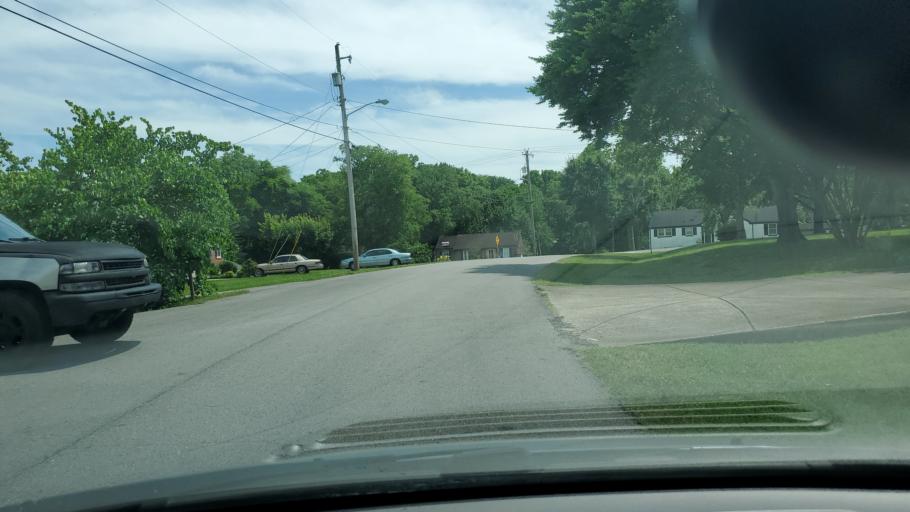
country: US
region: Tennessee
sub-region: Davidson County
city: Nashville
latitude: 36.2349
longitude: -86.7304
